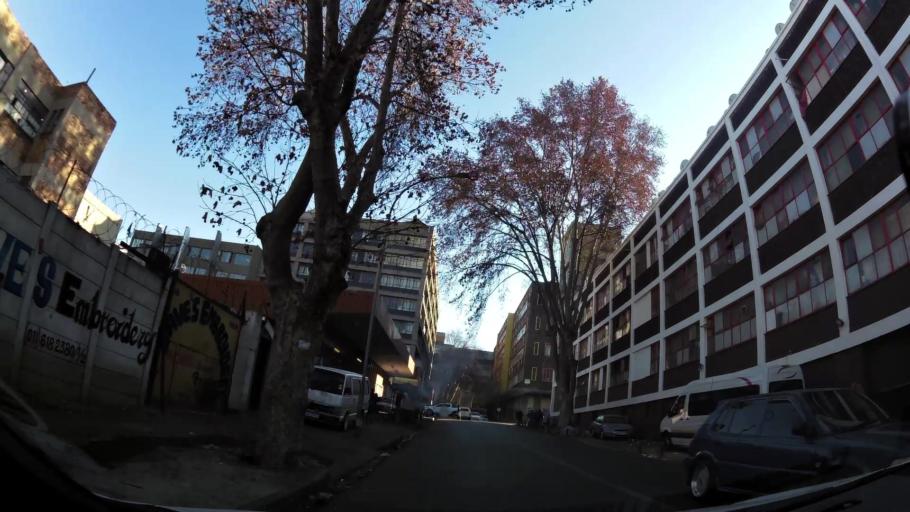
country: ZA
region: Gauteng
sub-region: City of Johannesburg Metropolitan Municipality
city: Johannesburg
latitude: -26.2052
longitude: 28.0600
